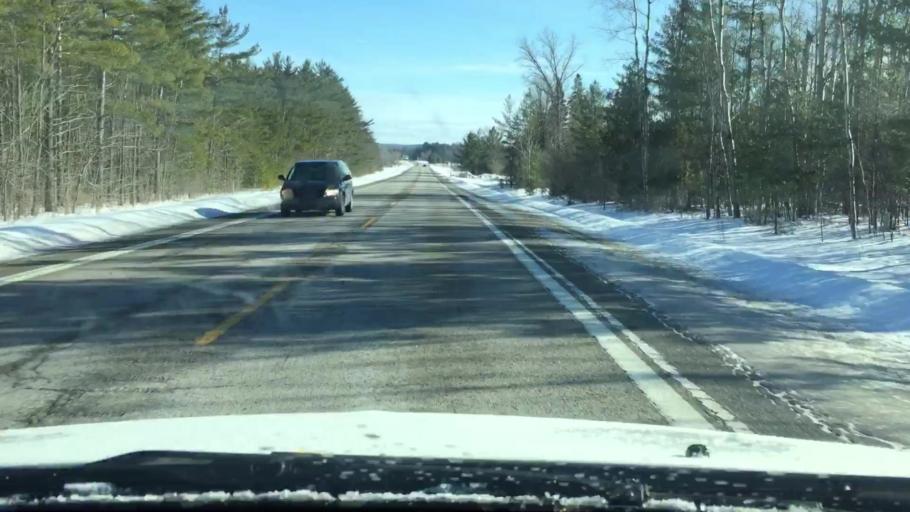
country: US
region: Michigan
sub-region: Charlevoix County
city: East Jordan
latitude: 45.1045
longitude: -85.1219
